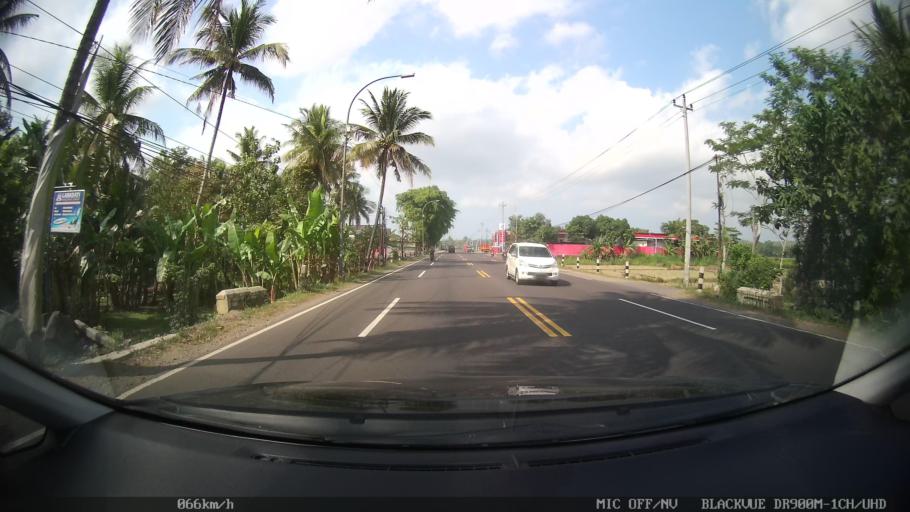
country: ID
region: Daerah Istimewa Yogyakarta
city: Srandakan
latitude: -7.8705
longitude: 110.2091
